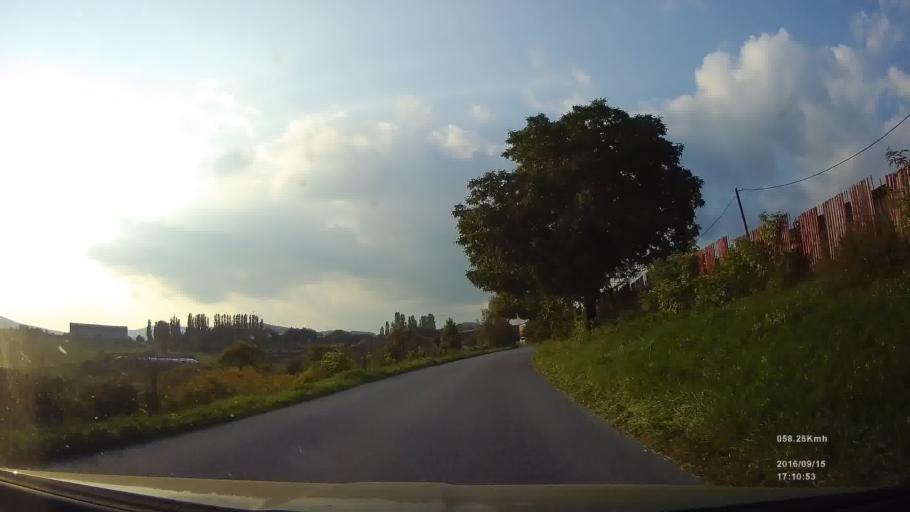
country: SK
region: Presovsky
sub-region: Okres Presov
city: Presov
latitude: 48.9178
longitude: 21.1095
